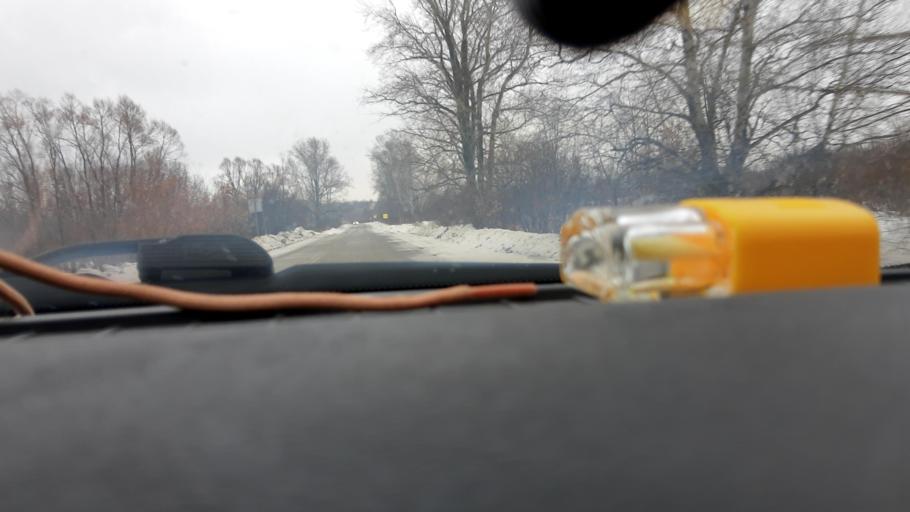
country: RU
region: Bashkortostan
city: Iglino
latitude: 54.6869
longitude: 56.4142
